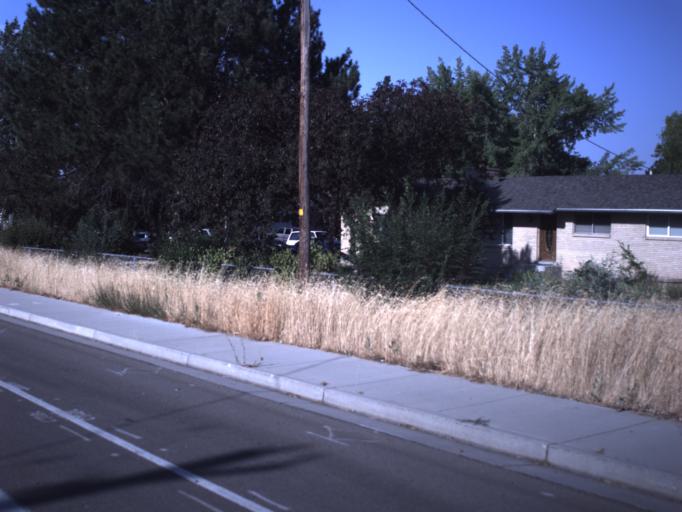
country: US
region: Utah
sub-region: Utah County
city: Cedar Hills
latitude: 40.4228
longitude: -111.7864
